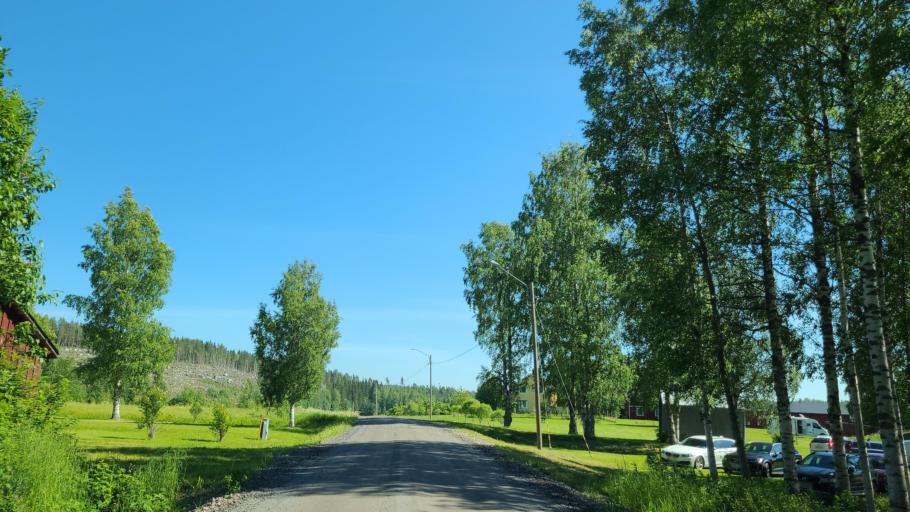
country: SE
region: Vaesterbotten
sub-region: Bjurholms Kommun
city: Bjurholm
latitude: 63.6684
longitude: 19.0696
